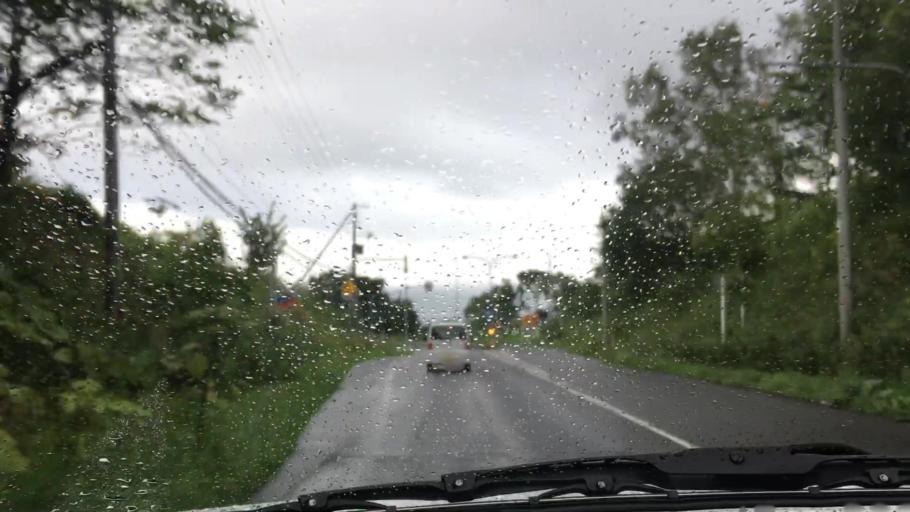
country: JP
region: Hokkaido
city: Date
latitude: 42.5922
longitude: 140.7210
